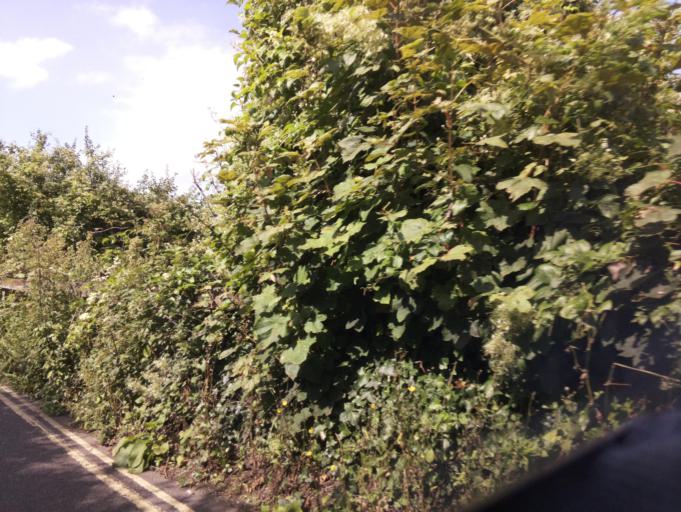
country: GB
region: England
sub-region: Devon
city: Dartmouth
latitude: 50.3514
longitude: -3.5663
